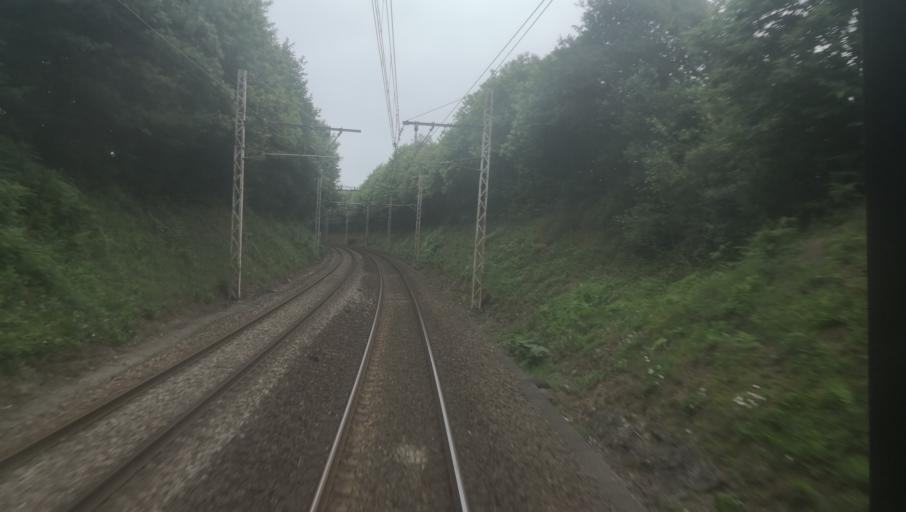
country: FR
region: Limousin
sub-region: Departement de la Creuse
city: Saint-Agnant-de-Versillat
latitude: 46.3323
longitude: 1.5368
